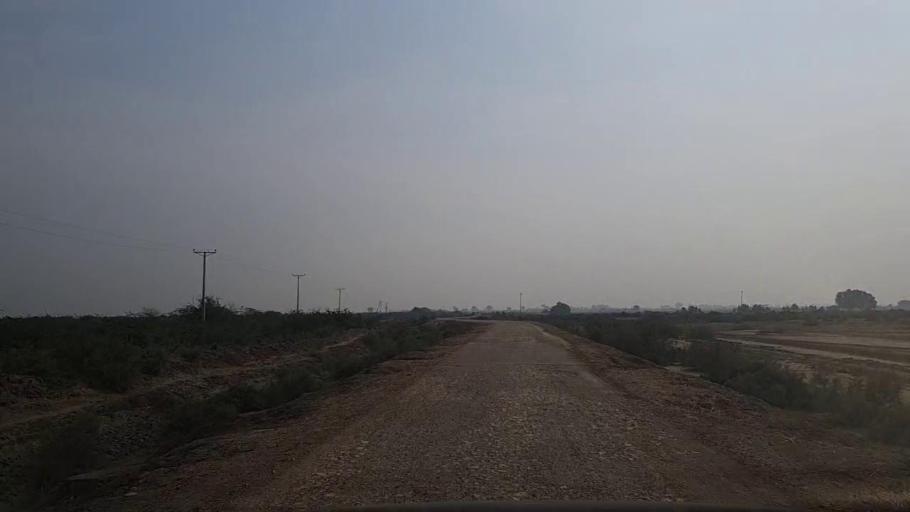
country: PK
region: Sindh
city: Mirpur Sakro
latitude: 24.3863
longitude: 67.7527
